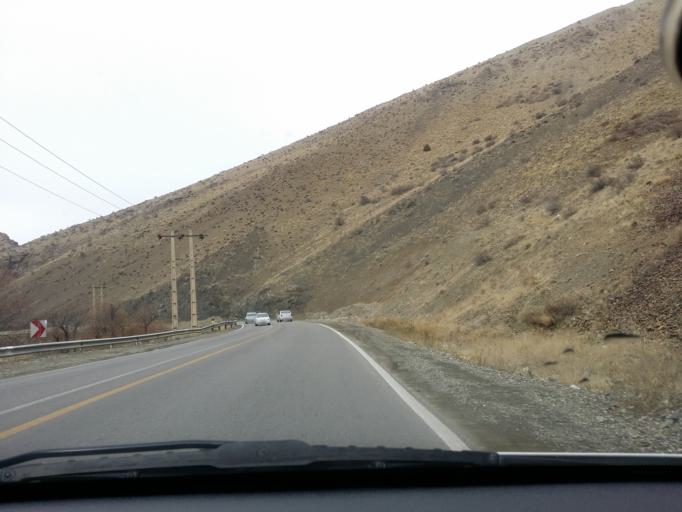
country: IR
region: Tehran
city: Tajrish
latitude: 36.0151
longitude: 51.2854
